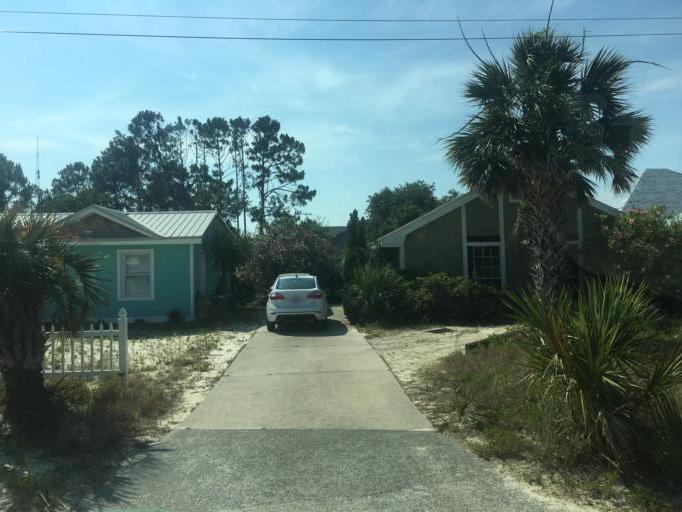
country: US
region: Florida
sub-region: Bay County
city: Panama City Beach
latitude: 30.1665
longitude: -85.7857
